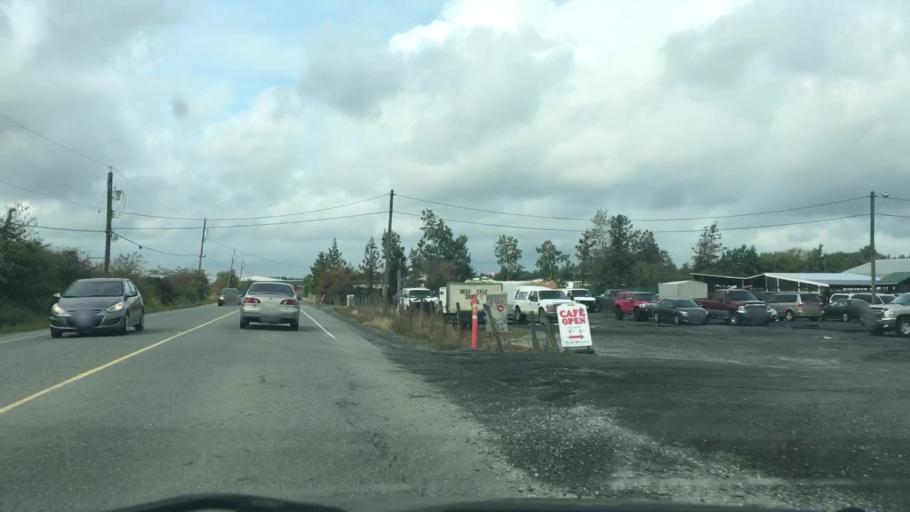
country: CA
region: British Columbia
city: Langley
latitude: 49.1041
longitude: -122.6180
